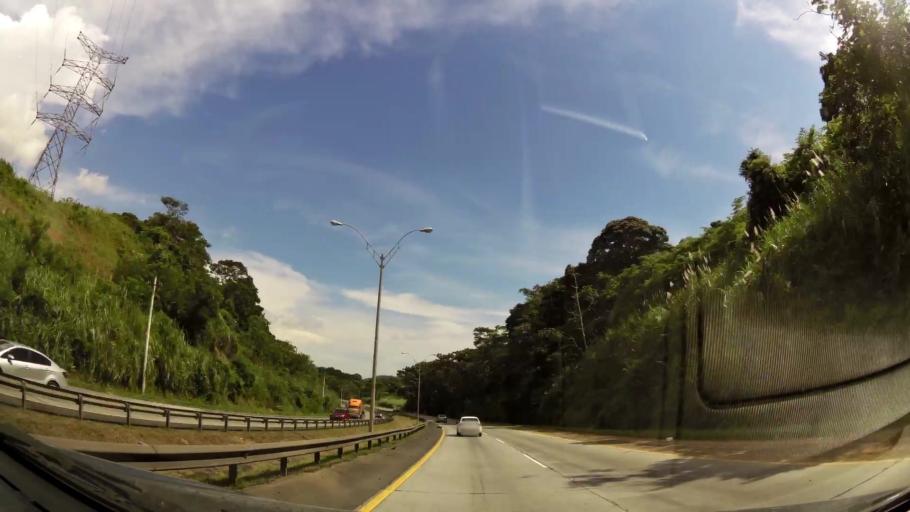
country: PA
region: Panama
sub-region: Distrito de Panama
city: Paraiso
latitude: 9.0282
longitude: -79.6130
